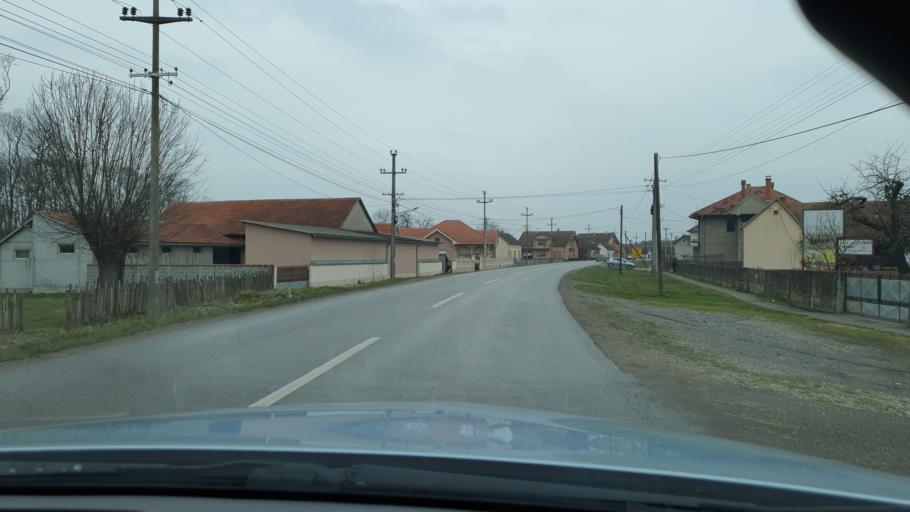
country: RS
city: Belotic
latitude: 44.8144
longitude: 19.5495
